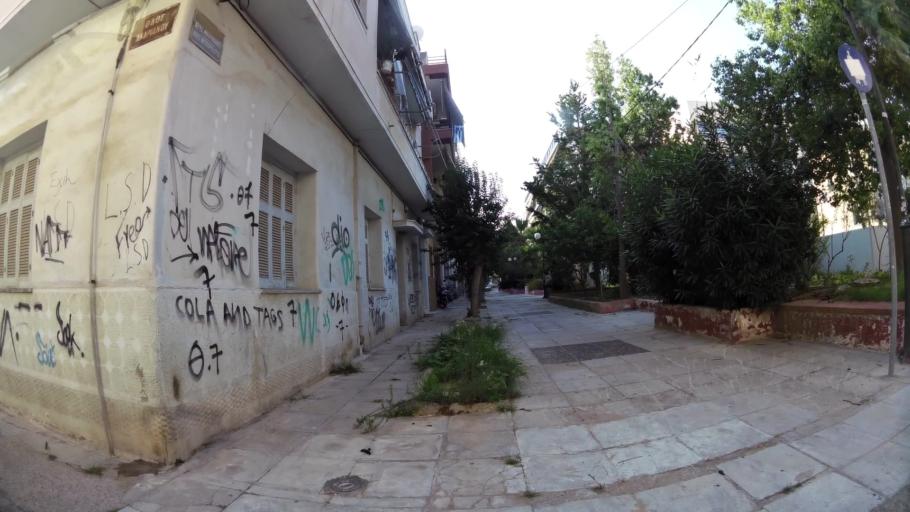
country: GR
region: Attica
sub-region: Nomos Piraios
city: Drapetsona
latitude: 37.9528
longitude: 23.6269
